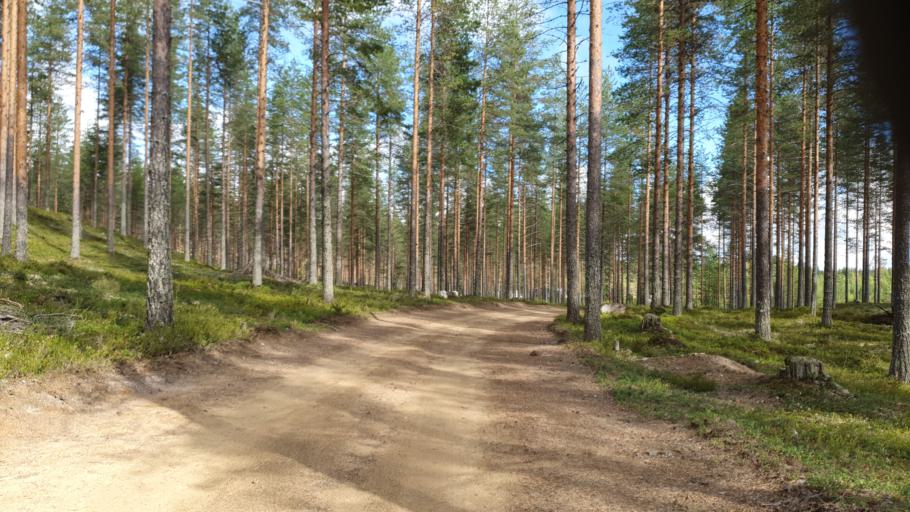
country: FI
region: Kainuu
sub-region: Kehys-Kainuu
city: Kuhmo
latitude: 64.1492
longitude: 29.3848
